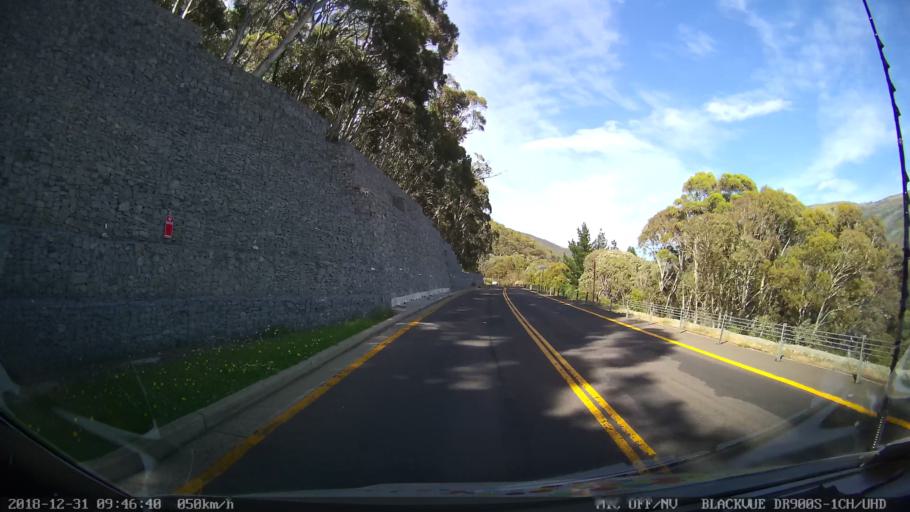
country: AU
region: New South Wales
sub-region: Snowy River
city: Jindabyne
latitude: -36.5048
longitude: 148.3076
